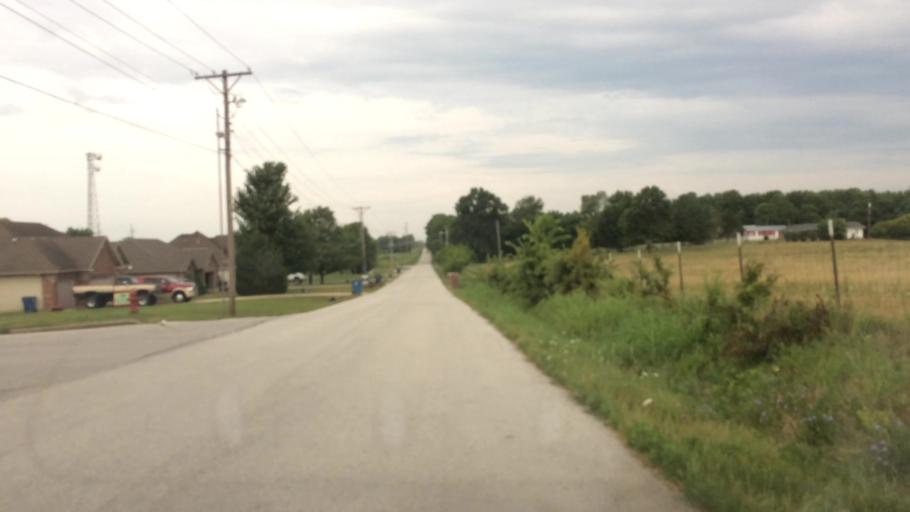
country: US
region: Missouri
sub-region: Greene County
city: Strafford
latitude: 37.2709
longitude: -93.1330
